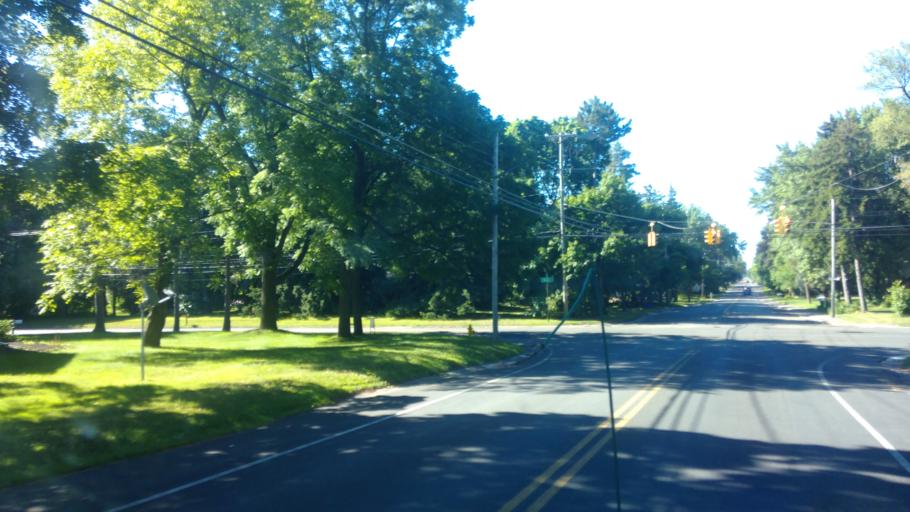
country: US
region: New York
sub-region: Monroe County
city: Webster
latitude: 43.2310
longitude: -77.4614
